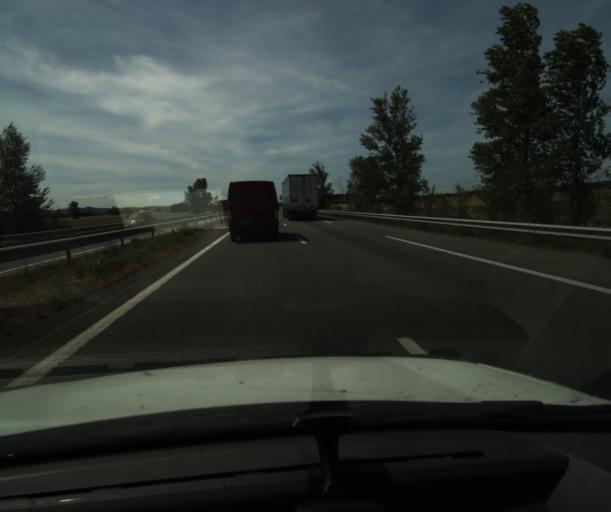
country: FR
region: Languedoc-Roussillon
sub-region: Departement de l'Aude
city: Saint-Martin-Lalande
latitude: 43.2576
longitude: 2.0321
